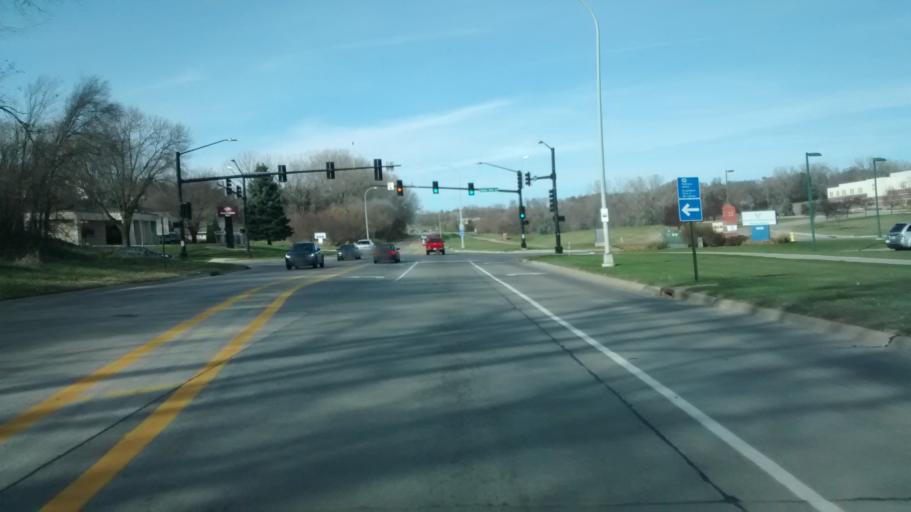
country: US
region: Iowa
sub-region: Woodbury County
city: Sioux City
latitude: 42.5364
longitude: -96.3737
